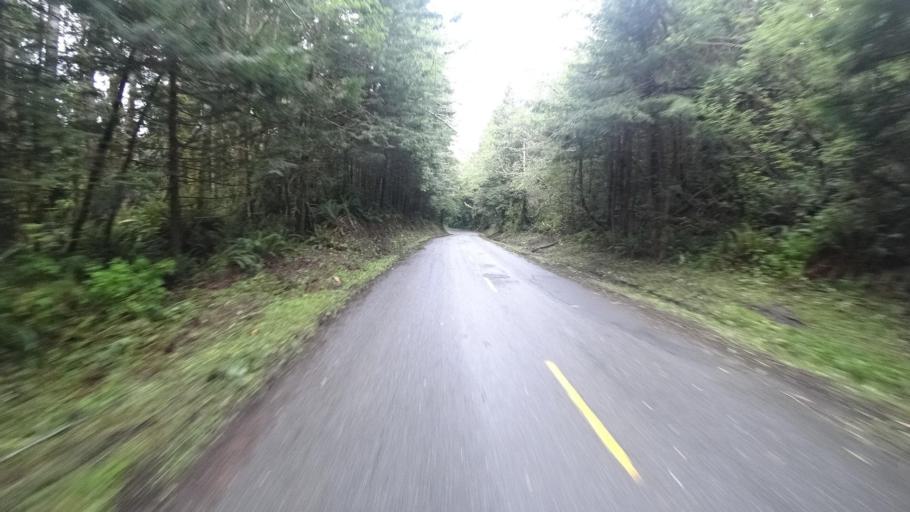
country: US
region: California
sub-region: Humboldt County
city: Westhaven-Moonstone
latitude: 41.3010
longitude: -124.0255
